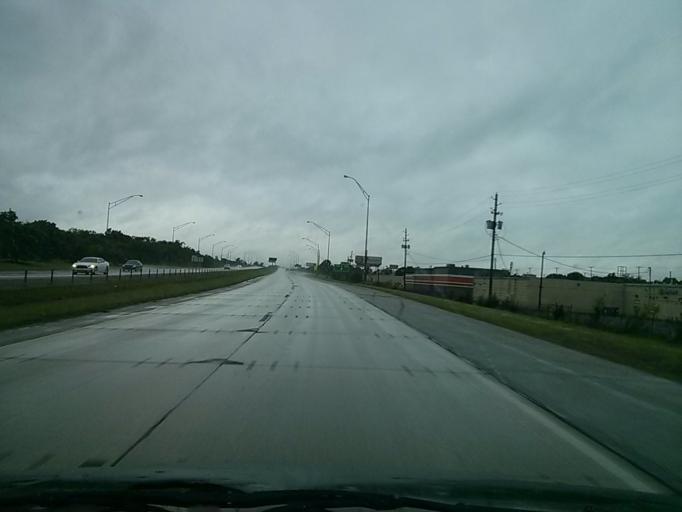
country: US
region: Oklahoma
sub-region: Tulsa County
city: Oakhurst
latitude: 36.1019
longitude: -96.0247
